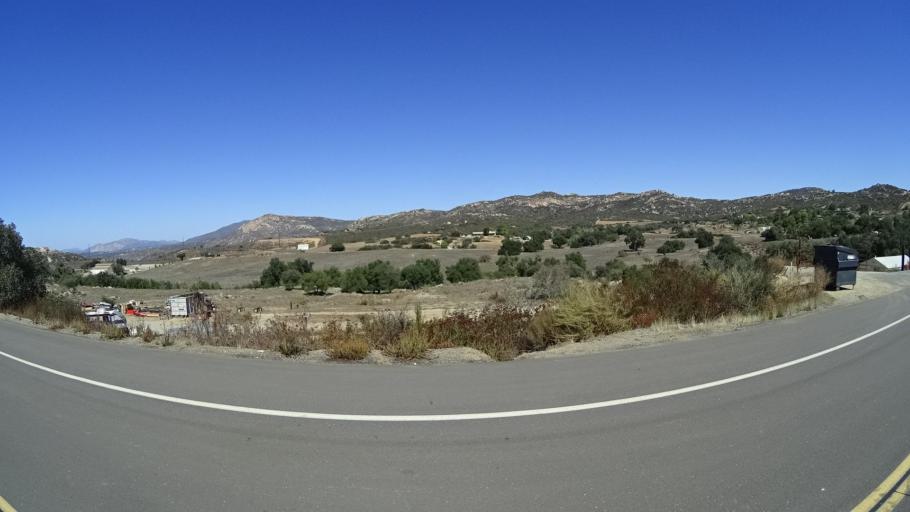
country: US
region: California
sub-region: San Diego County
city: Alpine
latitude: 32.7644
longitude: -116.6858
